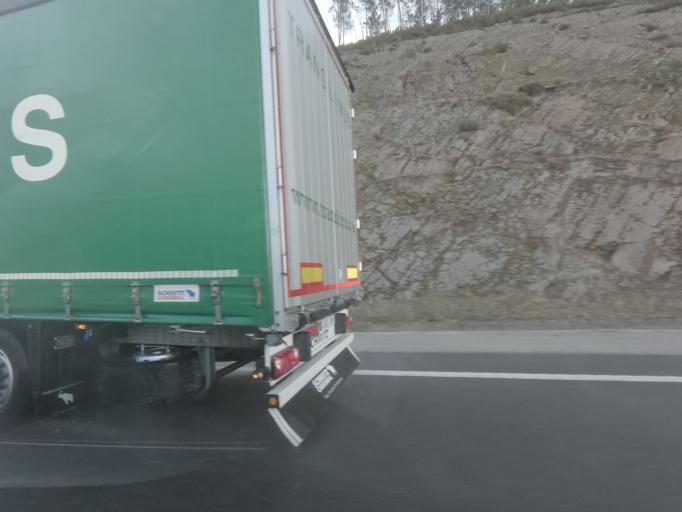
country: PT
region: Viseu
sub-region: Lamego
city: Lamego
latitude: 41.0481
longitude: -7.8592
